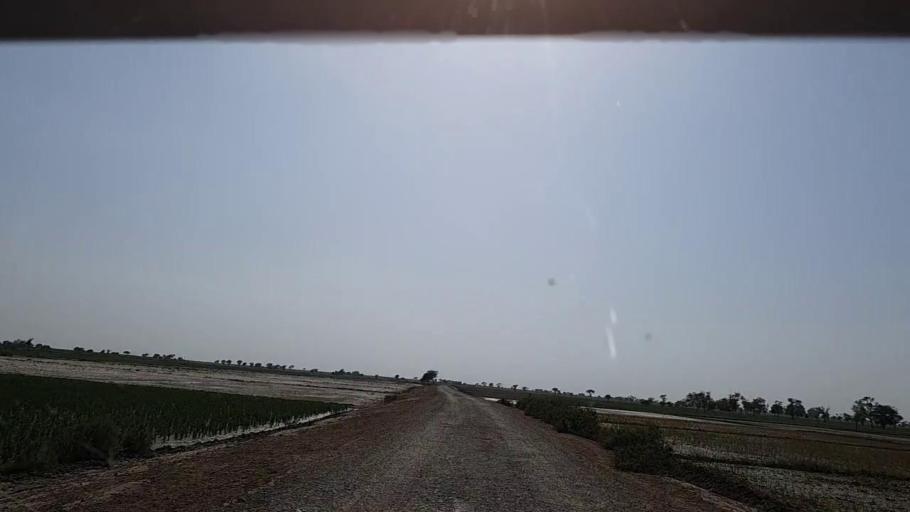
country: PK
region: Sindh
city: Phulji
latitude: 26.9218
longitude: 67.6702
